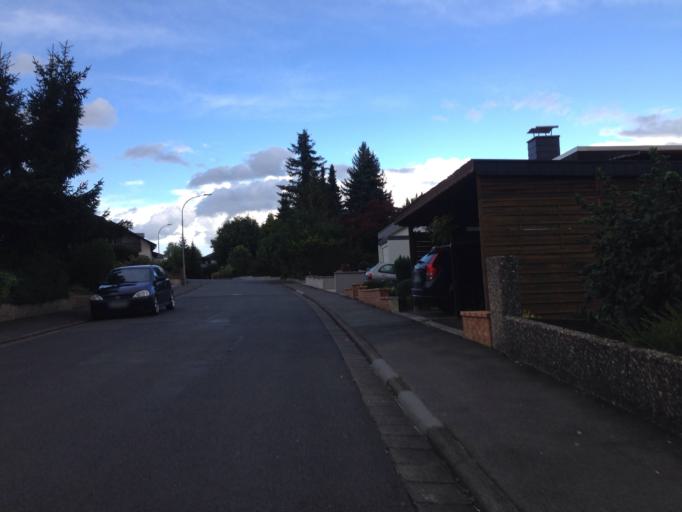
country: DE
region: Hesse
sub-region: Regierungsbezirk Giessen
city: Hungen
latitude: 50.4702
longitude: 8.8966
